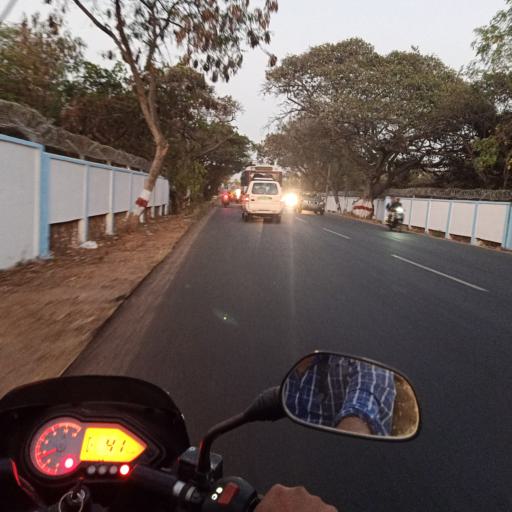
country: IN
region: Telangana
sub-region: Rangareddi
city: Secunderabad
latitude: 17.5574
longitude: 78.5410
